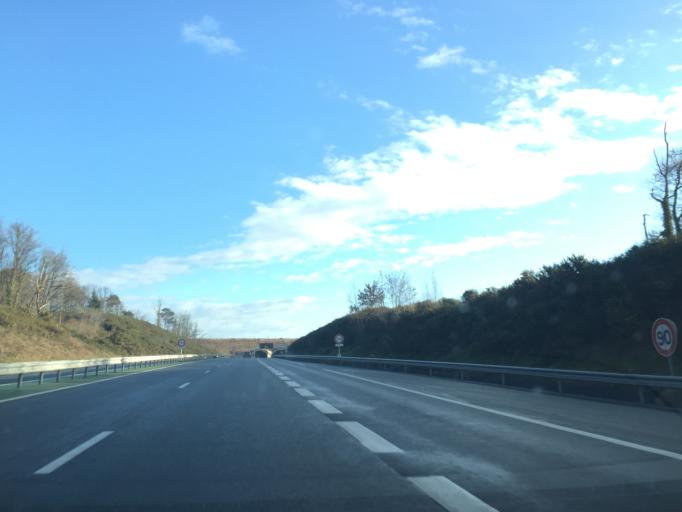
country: FR
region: Limousin
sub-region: Departement de la Correze
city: Cublac
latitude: 45.1638
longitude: 1.2280
